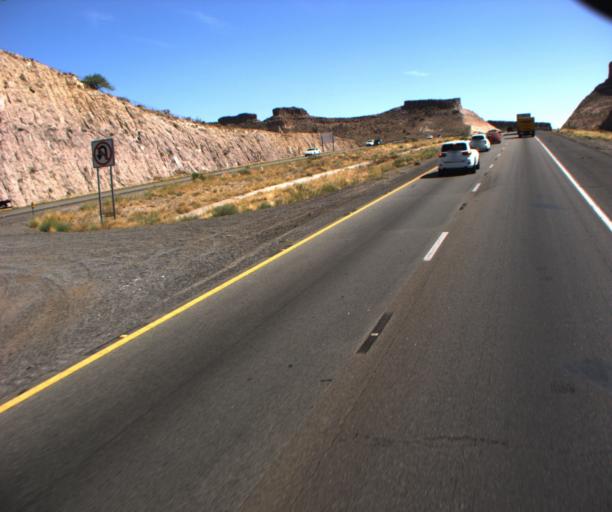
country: US
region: Arizona
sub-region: Mohave County
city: Kingman
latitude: 35.2048
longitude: -114.0620
